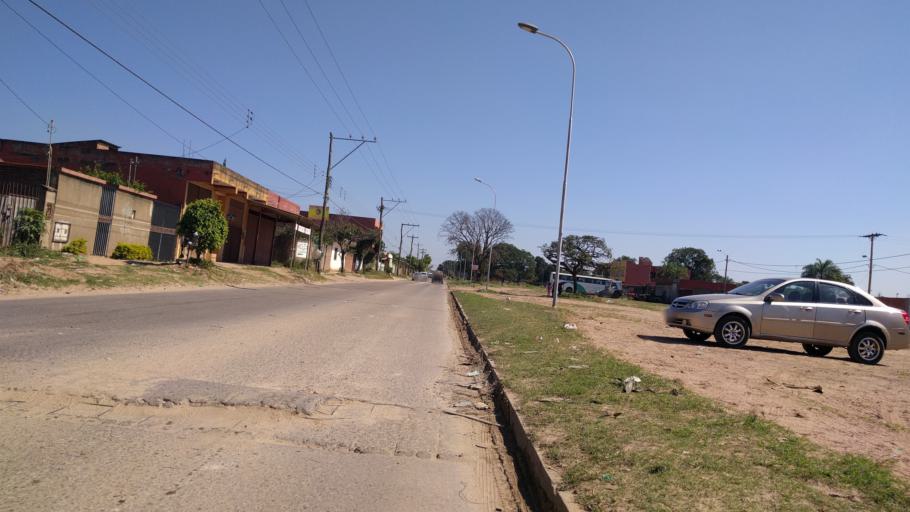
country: BO
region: Santa Cruz
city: Santa Cruz de la Sierra
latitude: -17.8502
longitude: -63.2023
